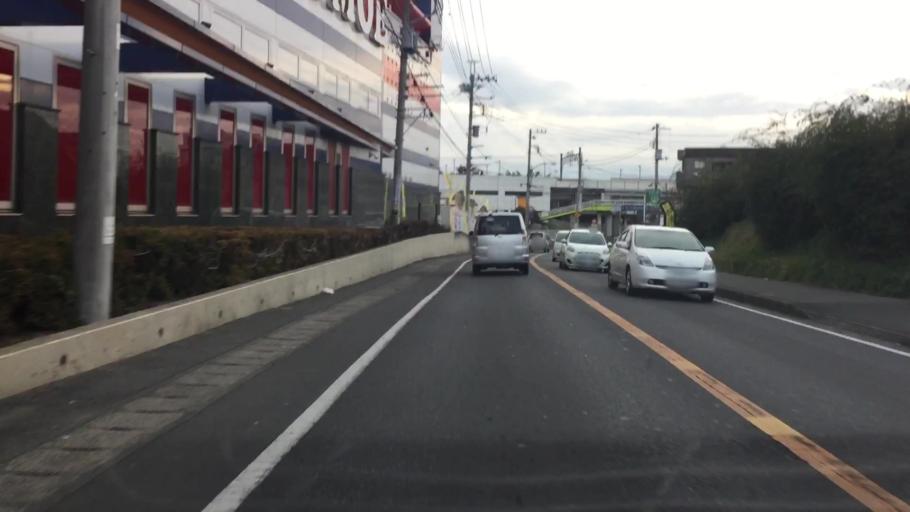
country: JP
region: Chiba
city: Matsudo
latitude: 35.7767
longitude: 139.9734
